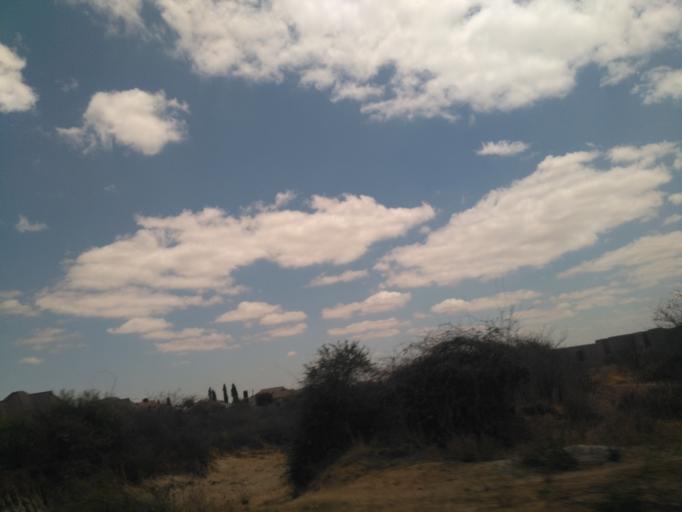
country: TZ
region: Dodoma
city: Kisasa
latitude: -6.1684
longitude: 35.7991
